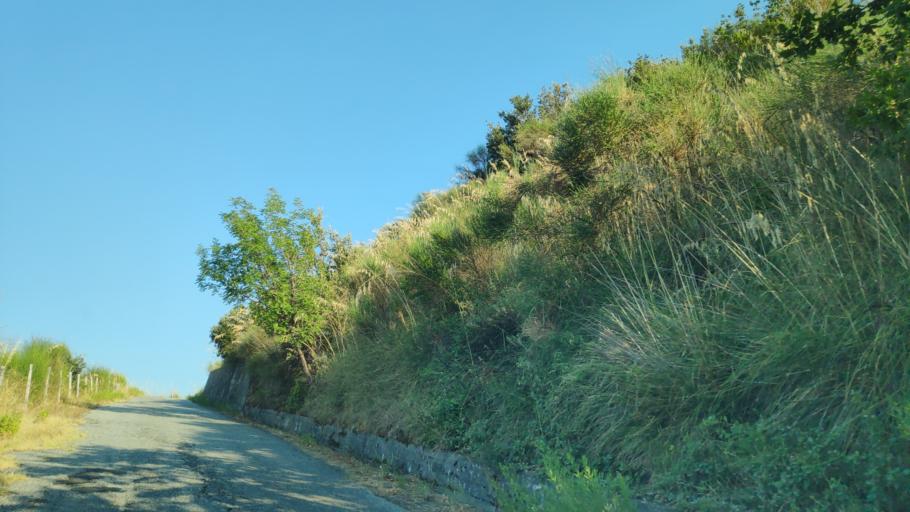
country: IT
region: Calabria
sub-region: Provincia di Reggio Calabria
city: Placanica
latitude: 38.4094
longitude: 16.4360
